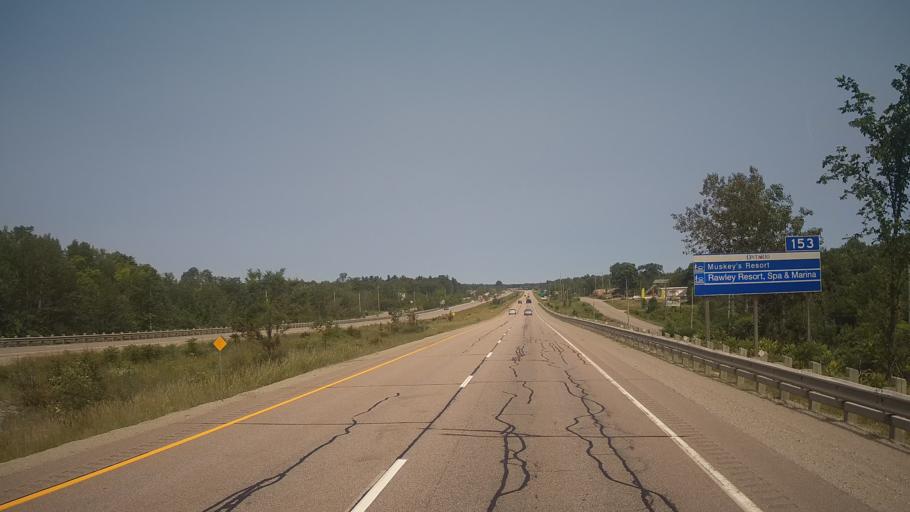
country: CA
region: Ontario
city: Midland
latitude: 44.7832
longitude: -79.6976
